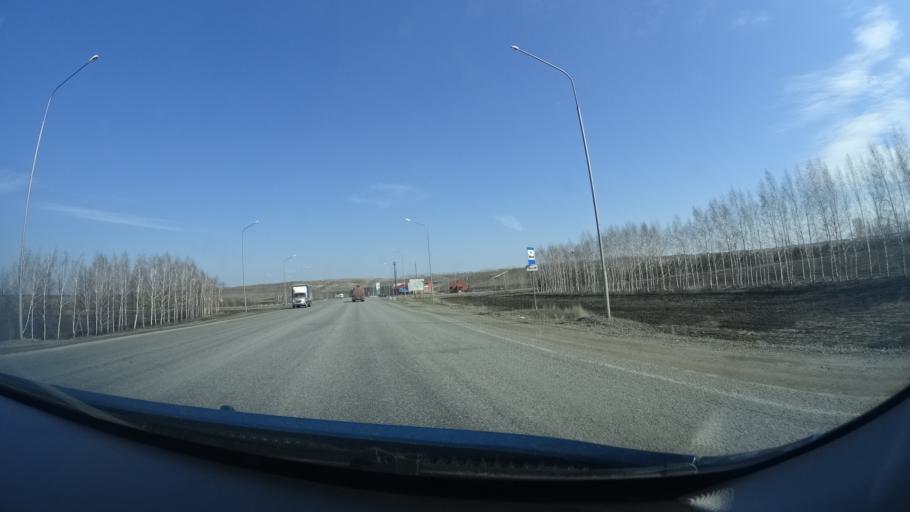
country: RU
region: Bashkortostan
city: Serafimovskiy
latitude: 54.4671
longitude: 53.7485
